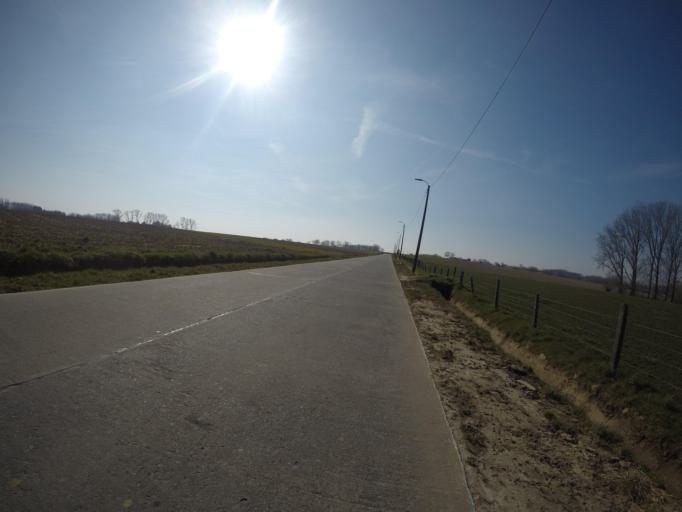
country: BE
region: Flanders
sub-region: Provincie Oost-Vlaanderen
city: Sint-Maria-Lierde
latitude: 50.7825
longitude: 3.8281
